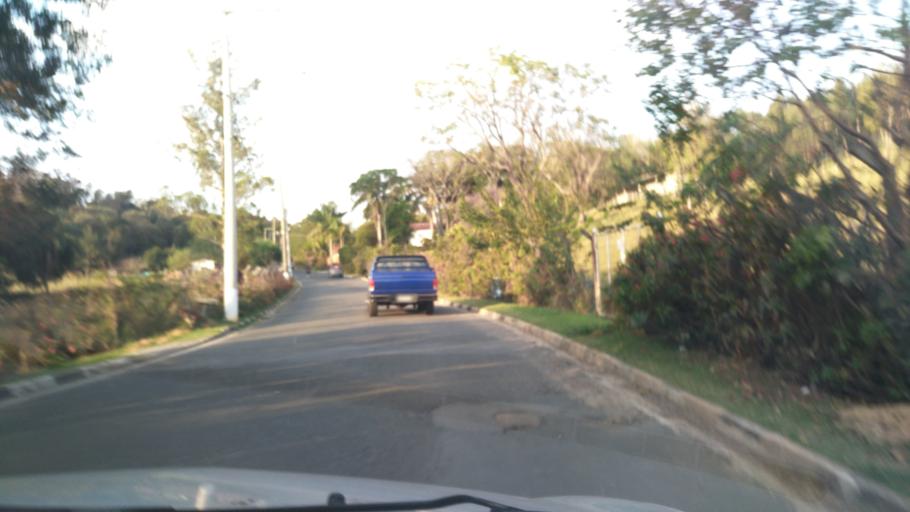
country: BR
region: Sao Paulo
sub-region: Vinhedo
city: Vinhedo
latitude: -23.0321
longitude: -47.0085
